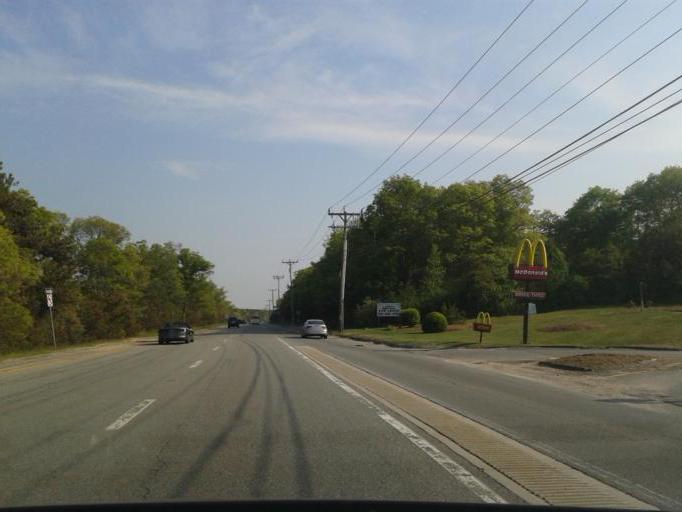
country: US
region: Massachusetts
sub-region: Barnstable County
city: Monument Beach
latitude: 41.7168
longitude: -70.5840
